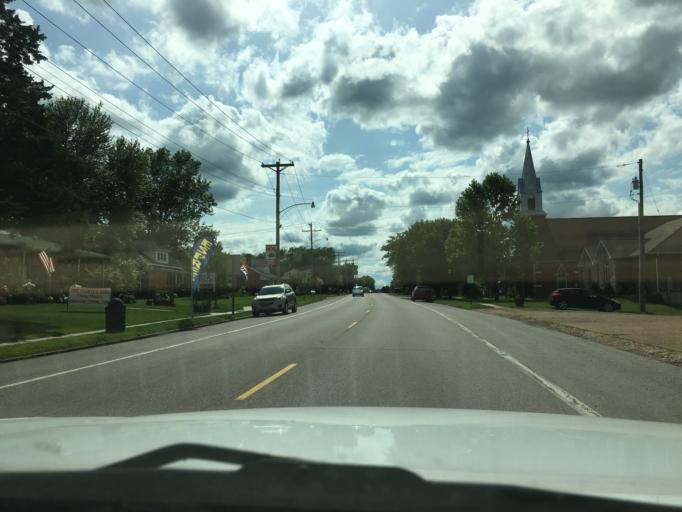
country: US
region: Missouri
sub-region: Franklin County
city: Gerald
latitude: 38.3872
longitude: -91.4013
